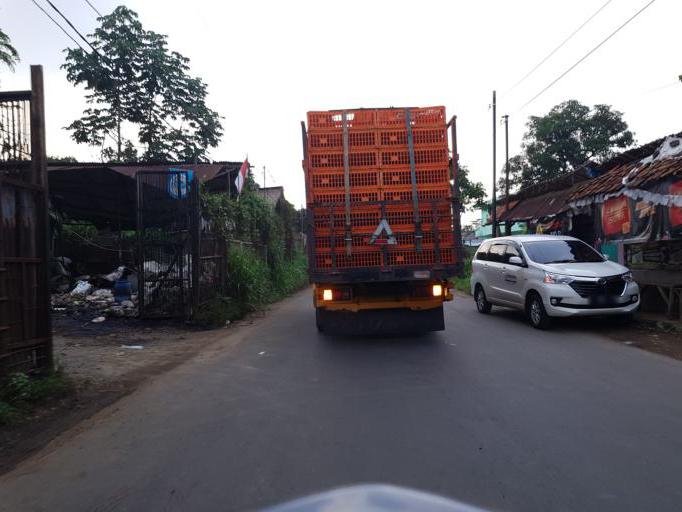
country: ID
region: West Java
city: Parung
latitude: -6.4756
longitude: 106.7280
